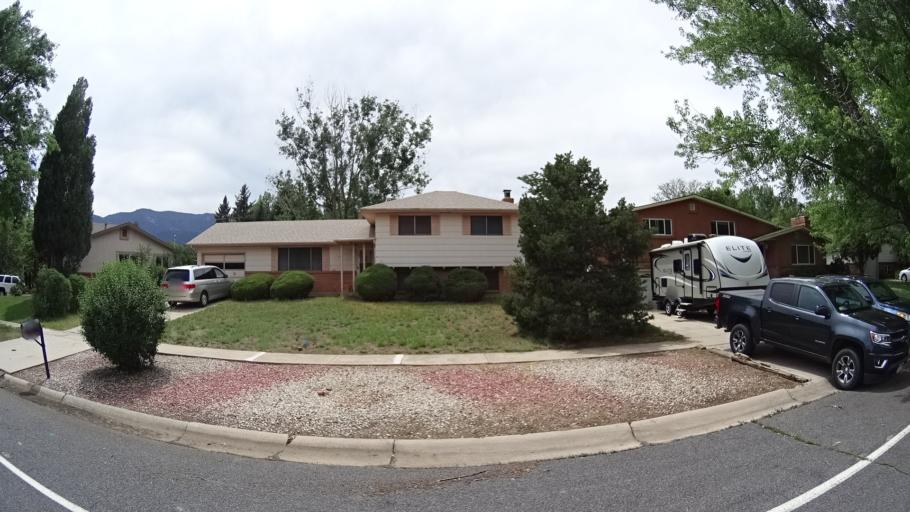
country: US
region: Colorado
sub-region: El Paso County
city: Manitou Springs
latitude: 38.8672
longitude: -104.8685
